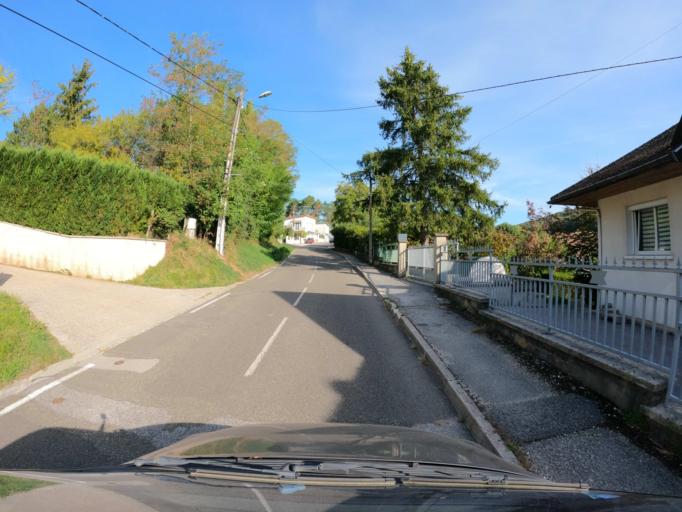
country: FR
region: Franche-Comte
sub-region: Departement du Jura
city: Montmorot
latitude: 46.6809
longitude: 5.5379
